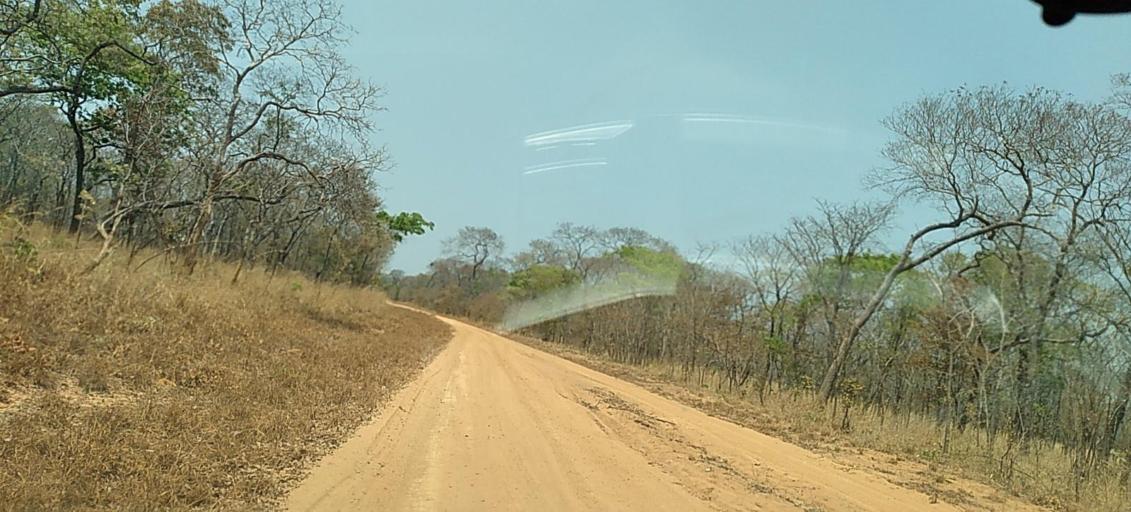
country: ZM
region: Central
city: Mumbwa
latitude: -14.3796
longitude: 26.4811
